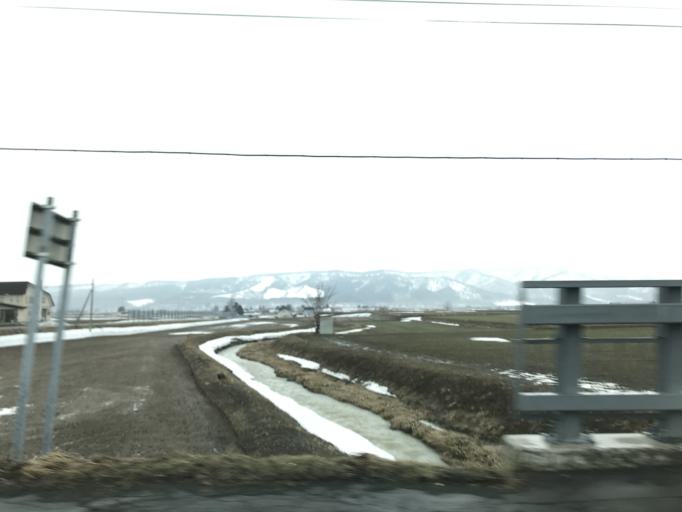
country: JP
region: Hokkaido
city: Nayoro
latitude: 44.2313
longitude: 142.3948
